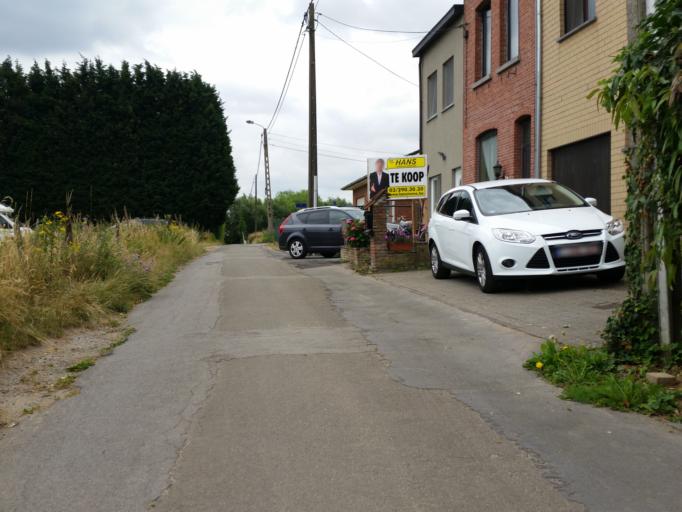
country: BE
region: Flanders
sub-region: Provincie Antwerpen
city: Mechelen
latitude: 51.0104
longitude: 4.4954
